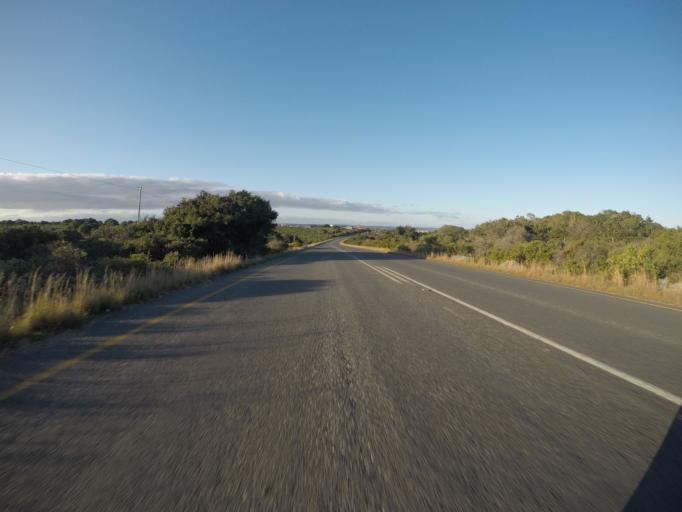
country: ZA
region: Western Cape
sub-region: Eden District Municipality
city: Riversdale
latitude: -34.3904
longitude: 21.3972
